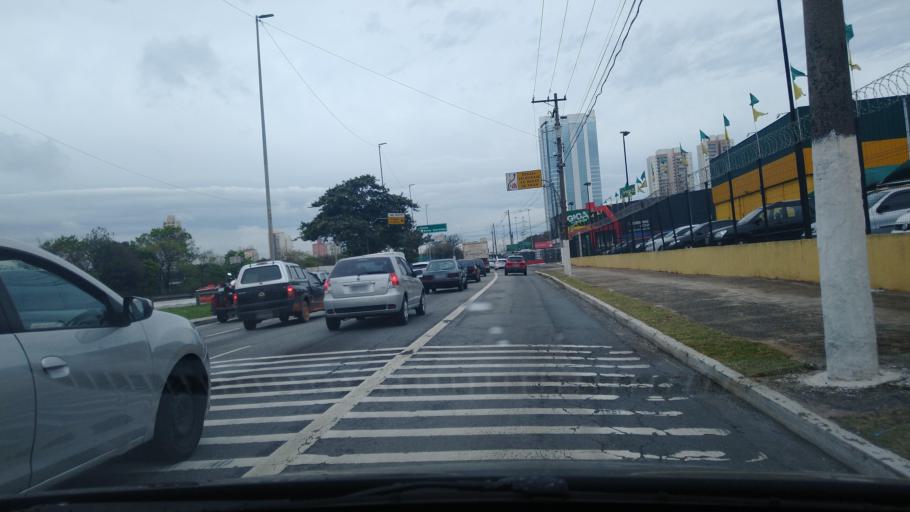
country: SA
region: Ar Riyad
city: Ad Dilam
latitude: 23.5157
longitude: 46.6706
